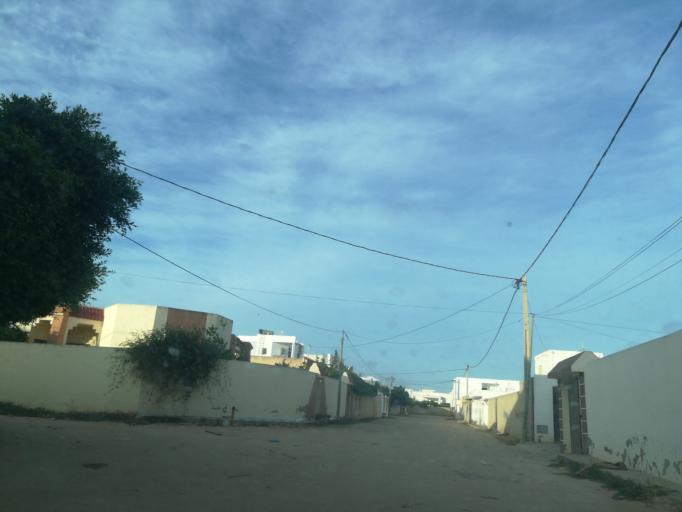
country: TN
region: Safaqis
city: Al Qarmadah
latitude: 34.8125
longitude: 10.7551
